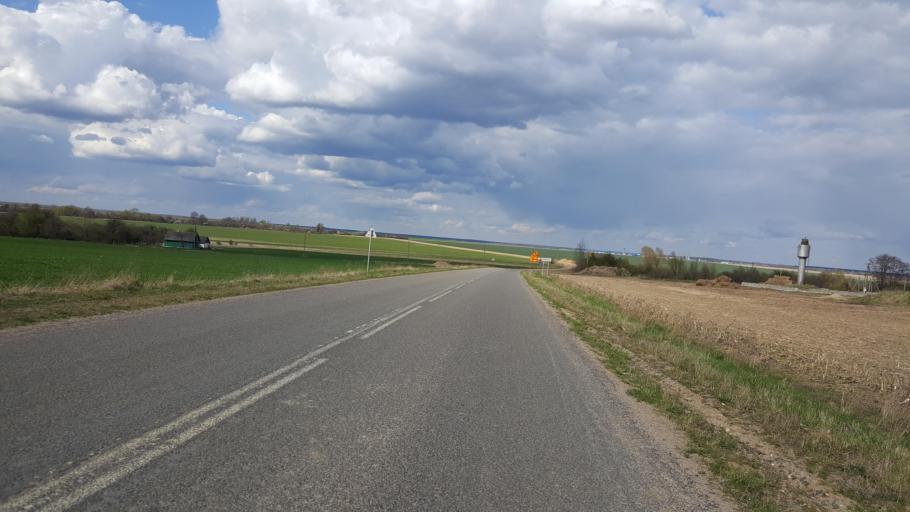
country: BY
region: Brest
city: Kamyanyets
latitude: 52.4405
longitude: 23.6530
